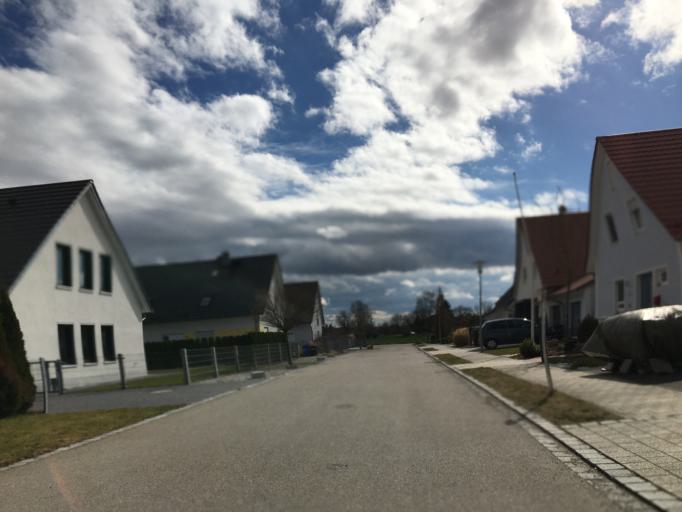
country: DE
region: Bavaria
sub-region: Upper Bavaria
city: Fuerstenfeldbruck
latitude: 48.1847
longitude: 11.2232
